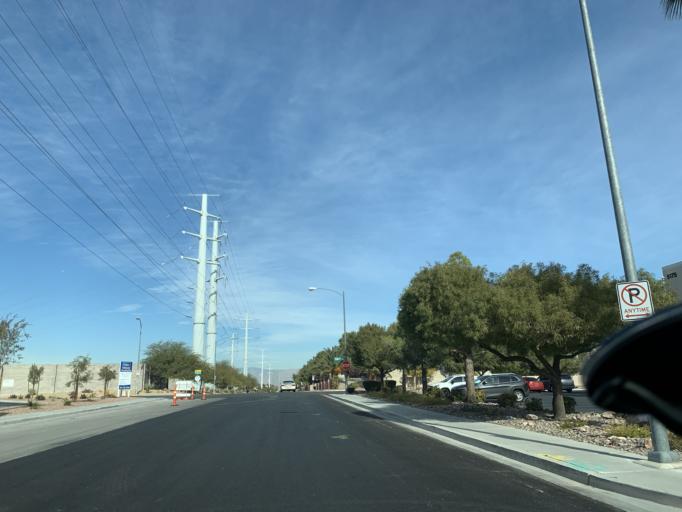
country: US
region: Nevada
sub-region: Clark County
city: Spring Valley
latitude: 36.0891
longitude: -115.2123
